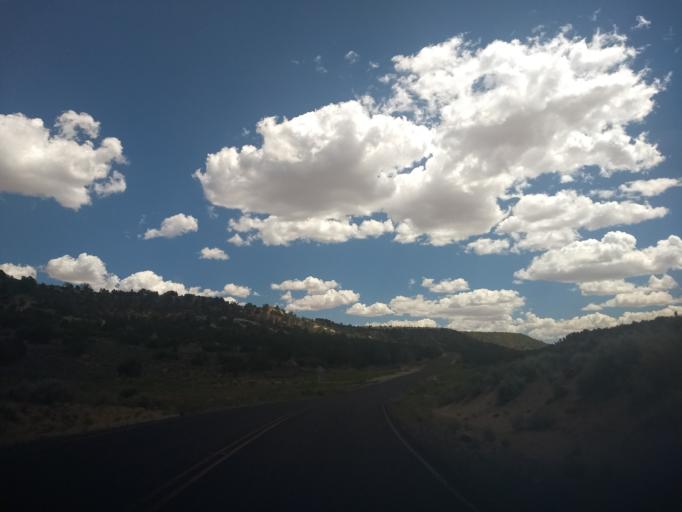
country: US
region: Utah
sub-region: Kane County
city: Kanab
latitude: 37.1202
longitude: -112.6766
